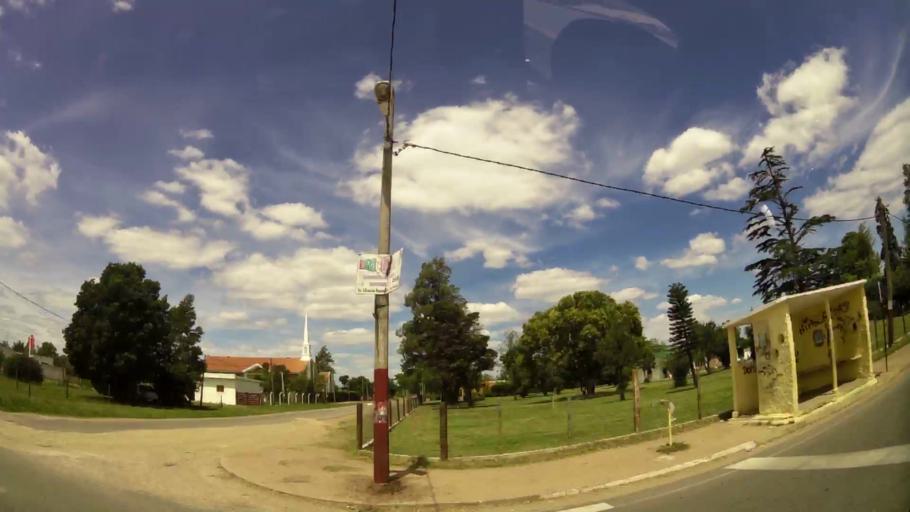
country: UY
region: San Jose
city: Delta del Tigre
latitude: -34.7447
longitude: -56.4522
